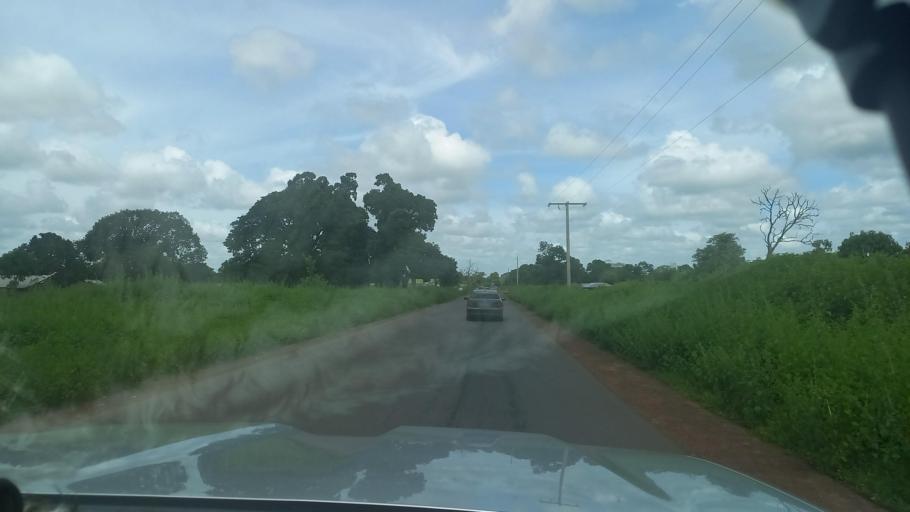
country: GM
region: Lower River
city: Kaiaf
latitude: 13.2027
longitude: -15.5503
